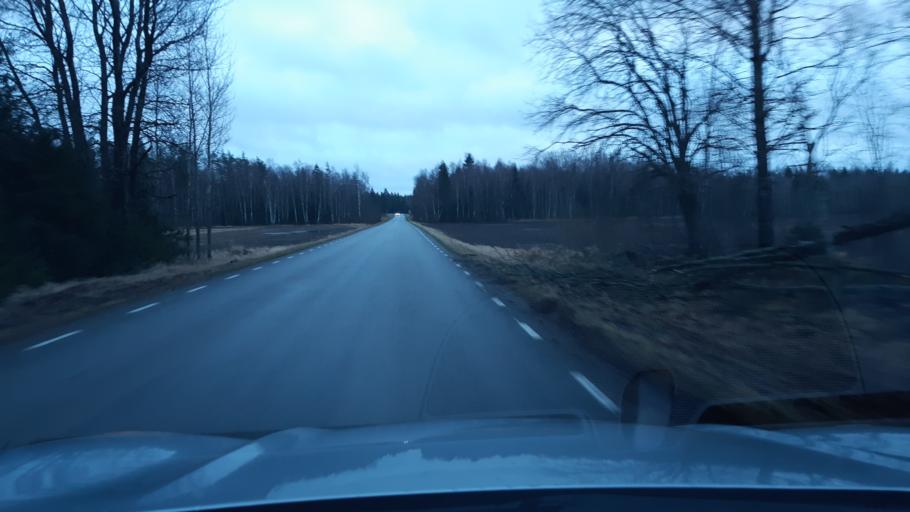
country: EE
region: Raplamaa
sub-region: Rapla vald
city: Rapla
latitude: 59.0296
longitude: 24.6791
